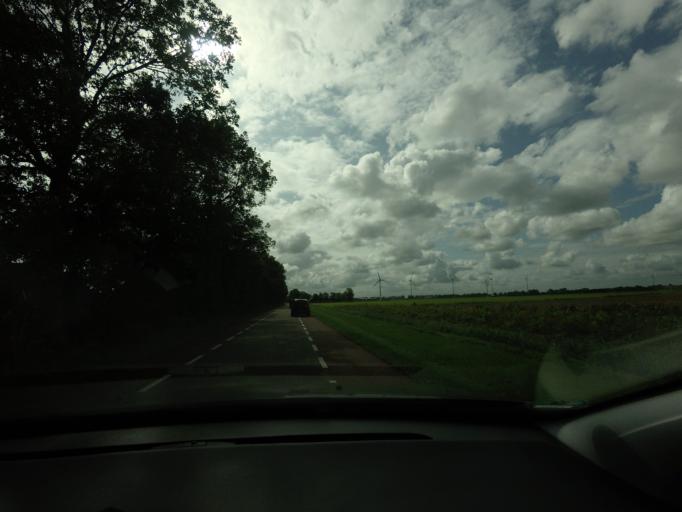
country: NL
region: North Holland
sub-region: Gemeente Medemblik
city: Medemblik
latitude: 52.8163
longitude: 5.1082
